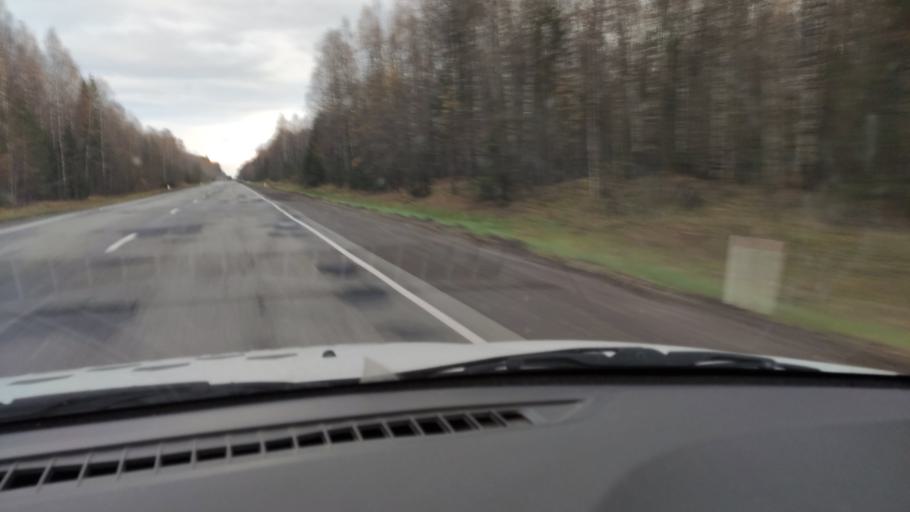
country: RU
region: Kirov
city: Omutninsk
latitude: 58.7669
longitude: 51.9762
